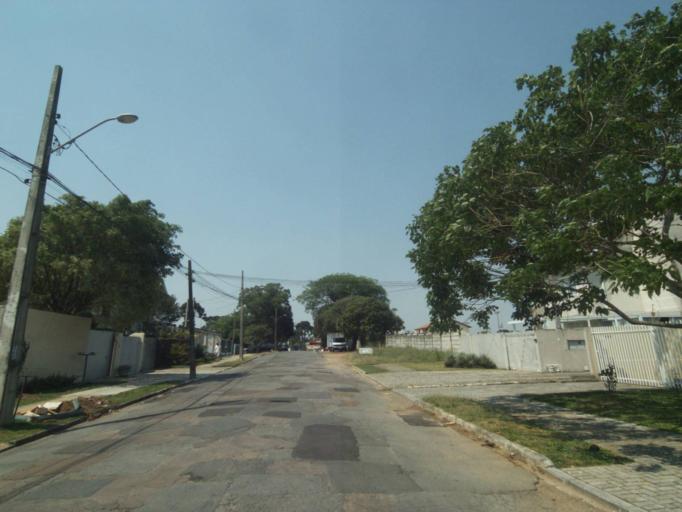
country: BR
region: Parana
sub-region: Sao Jose Dos Pinhais
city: Sao Jose dos Pinhais
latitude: -25.5119
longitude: -49.2615
